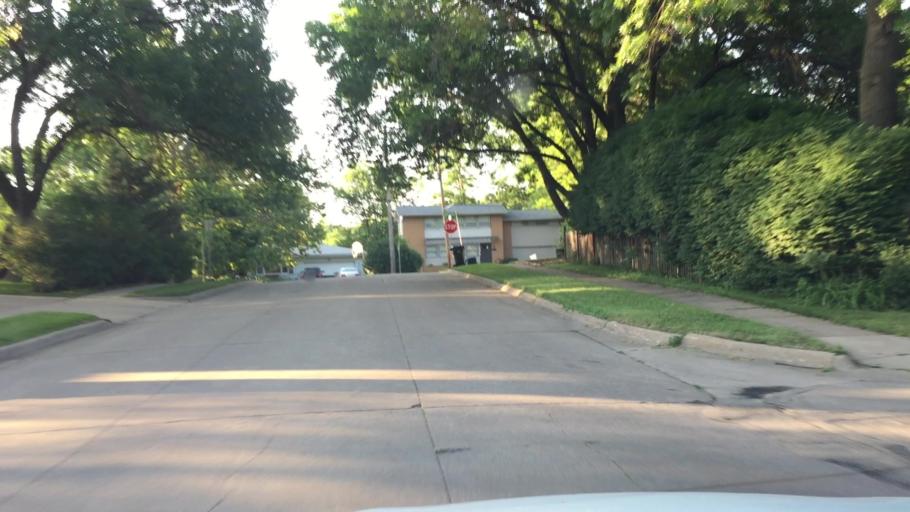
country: US
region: Iowa
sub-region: Johnson County
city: Iowa City
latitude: 41.6632
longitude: -91.5074
